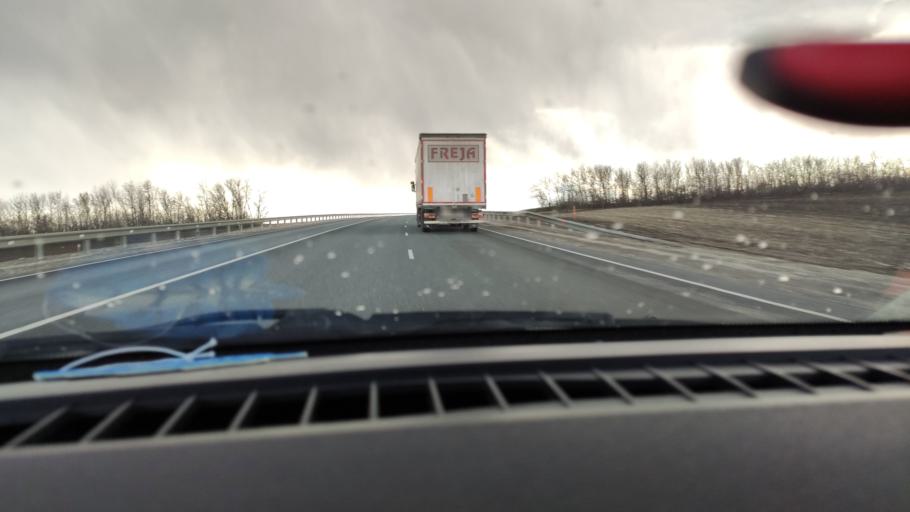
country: RU
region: Saratov
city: Yelshanka
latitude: 51.8340
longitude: 46.4672
